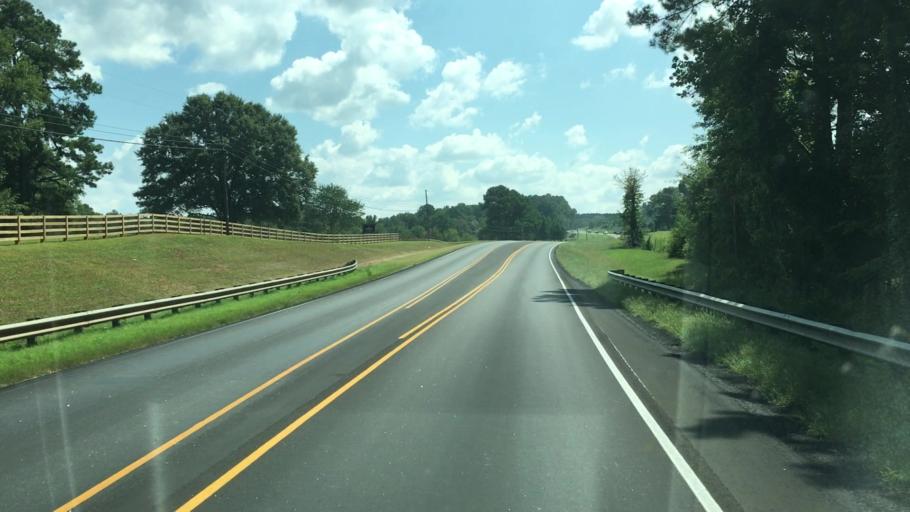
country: US
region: Georgia
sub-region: Morgan County
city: Madison
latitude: 33.6439
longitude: -83.4481
